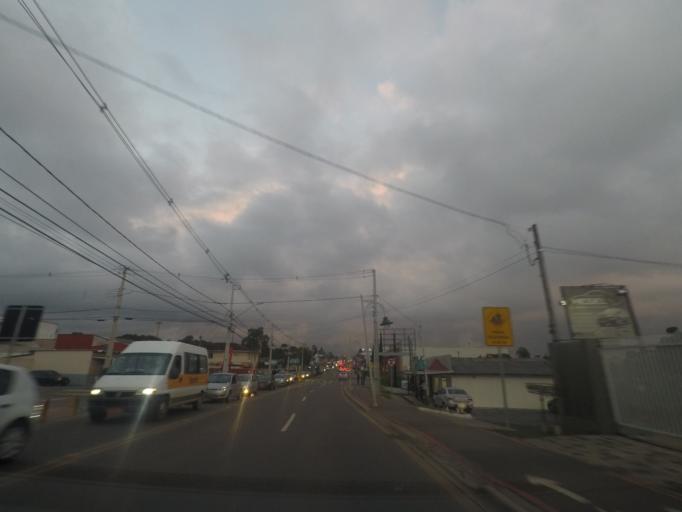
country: BR
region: Parana
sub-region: Almirante Tamandare
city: Almirante Tamandare
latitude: -25.3939
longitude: -49.3496
